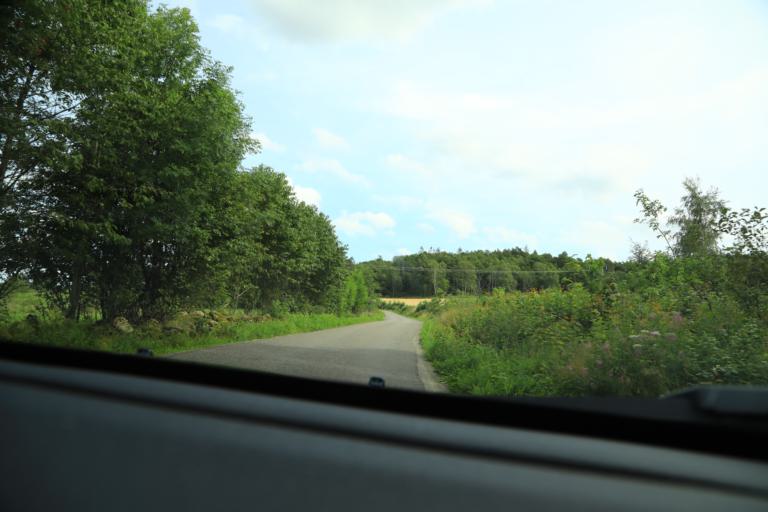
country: SE
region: Halland
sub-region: Varbergs Kommun
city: Varberg
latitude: 57.1758
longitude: 12.2643
